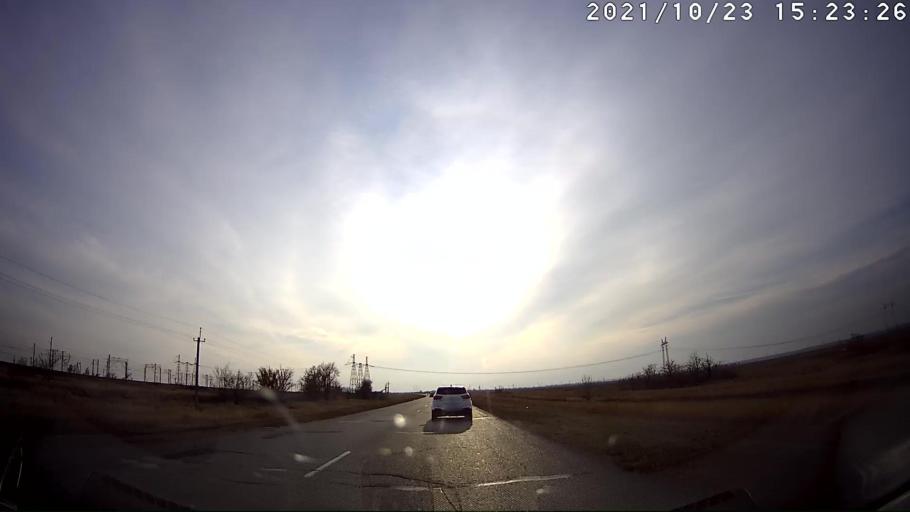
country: RU
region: Volgograd
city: Bereslavka
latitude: 48.2977
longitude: 44.2858
